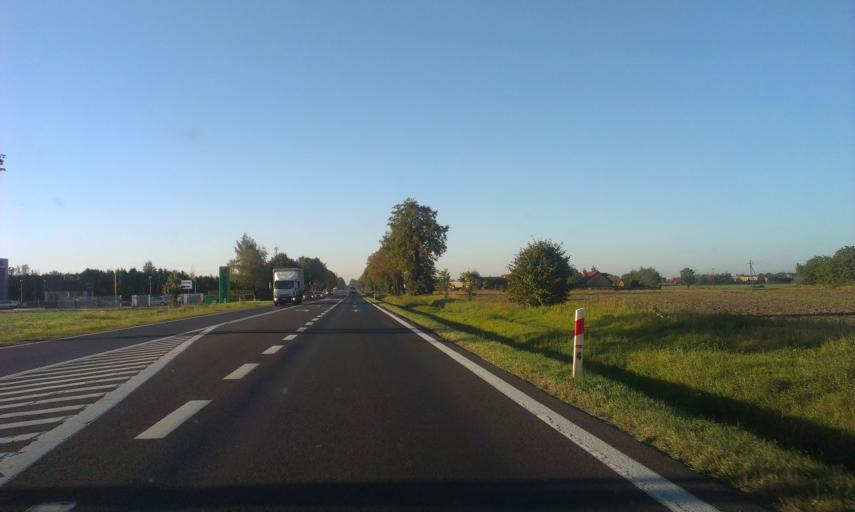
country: PL
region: Kujawsko-Pomorskie
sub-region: Powiat torunski
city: Lysomice
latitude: 53.0973
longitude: 18.6219
